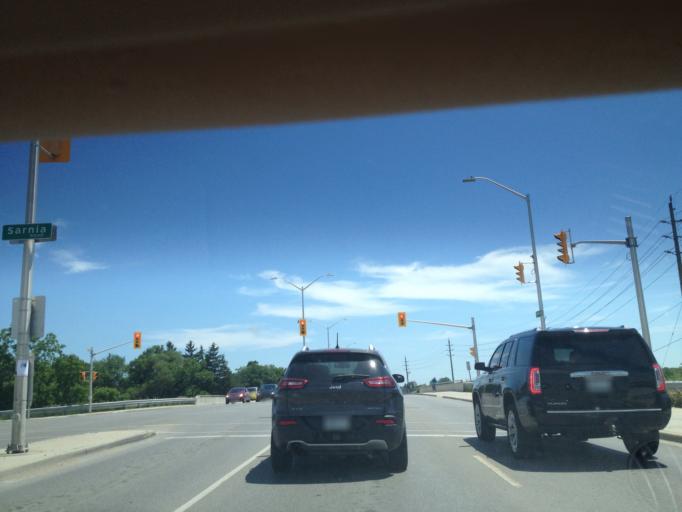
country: CA
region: Ontario
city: London
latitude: 42.9881
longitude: -81.3269
